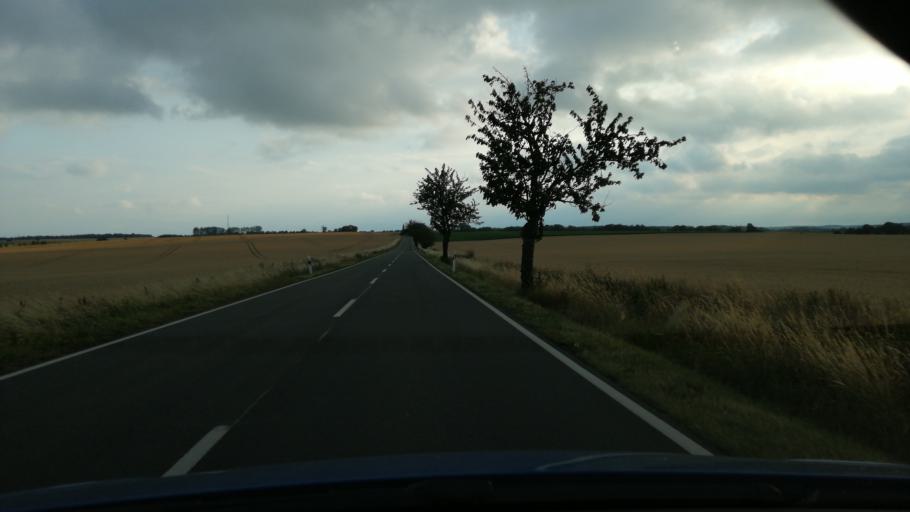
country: DE
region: Saxony-Anhalt
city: Mansfeld
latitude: 51.5737
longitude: 11.4529
